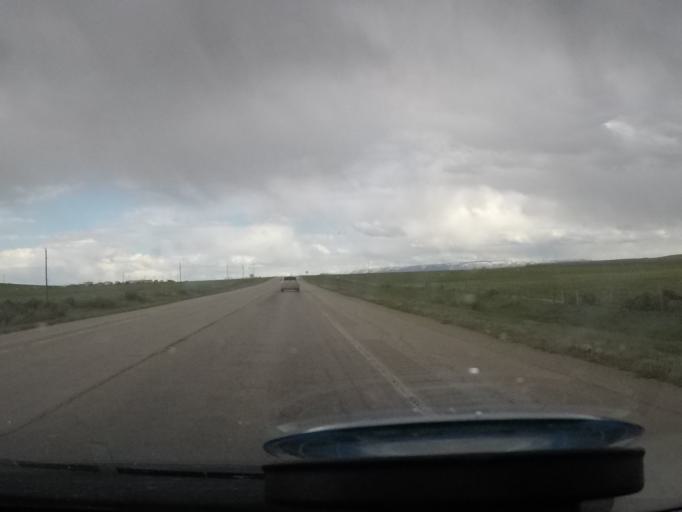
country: US
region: Wyoming
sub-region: Natrona County
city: Mills
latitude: 42.9579
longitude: -106.6532
